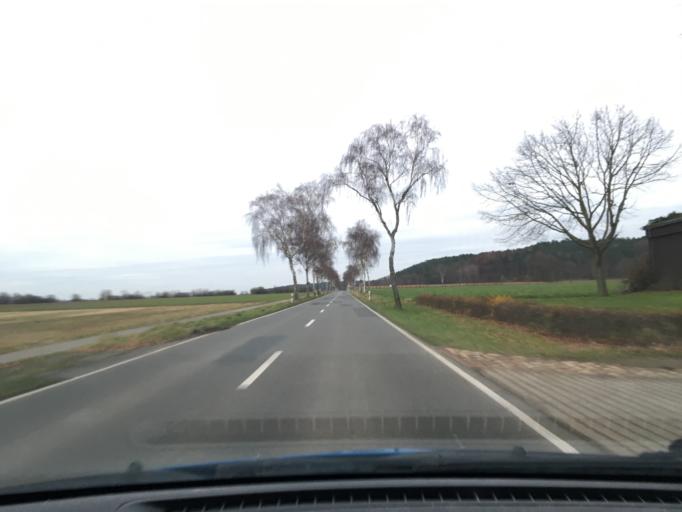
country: DE
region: Lower Saxony
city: Neu Darchau
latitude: 53.2369
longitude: 10.8566
